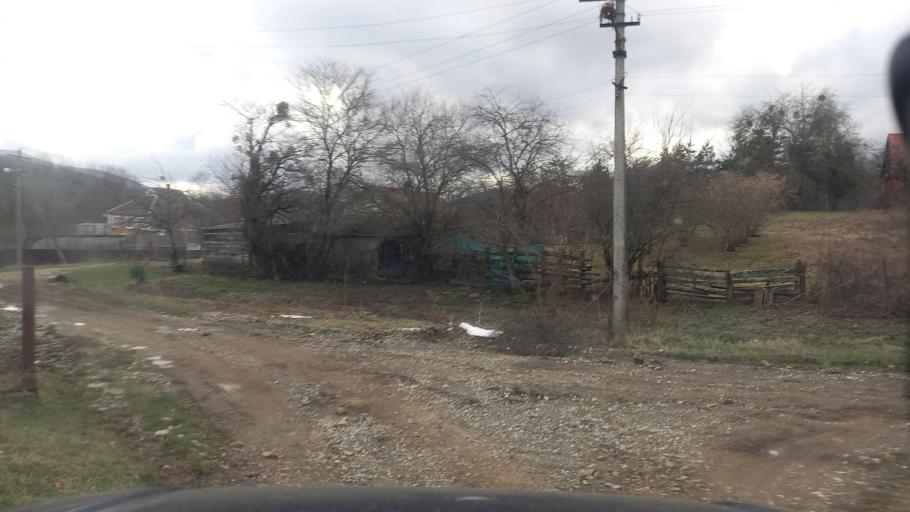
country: RU
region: Krasnodarskiy
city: Smolenskaya
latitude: 44.5668
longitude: 38.8040
